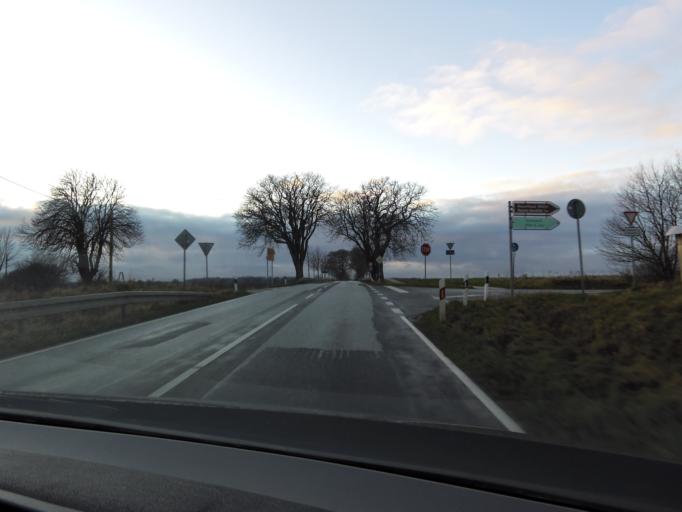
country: DE
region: Mecklenburg-Vorpommern
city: Gadebusch
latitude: 53.6954
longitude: 11.0702
